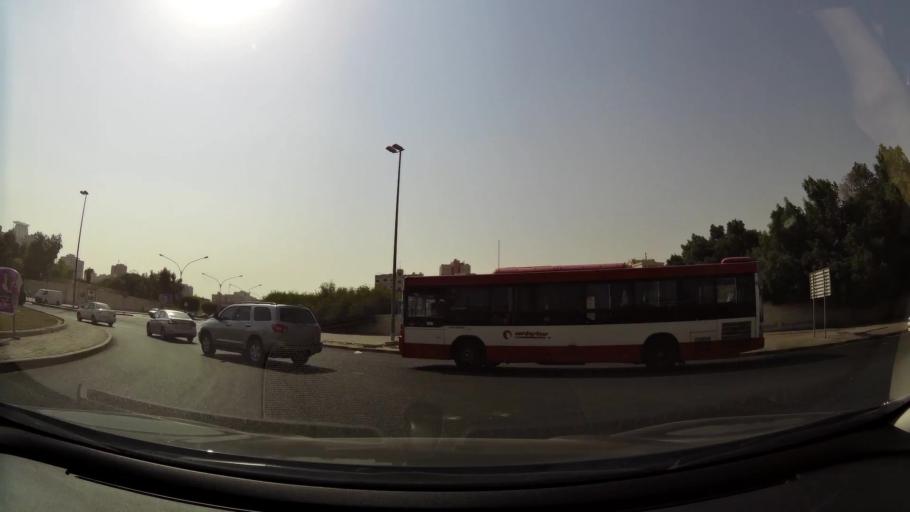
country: KW
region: Al Ahmadi
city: Al Fahahil
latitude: 29.0833
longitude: 48.1333
